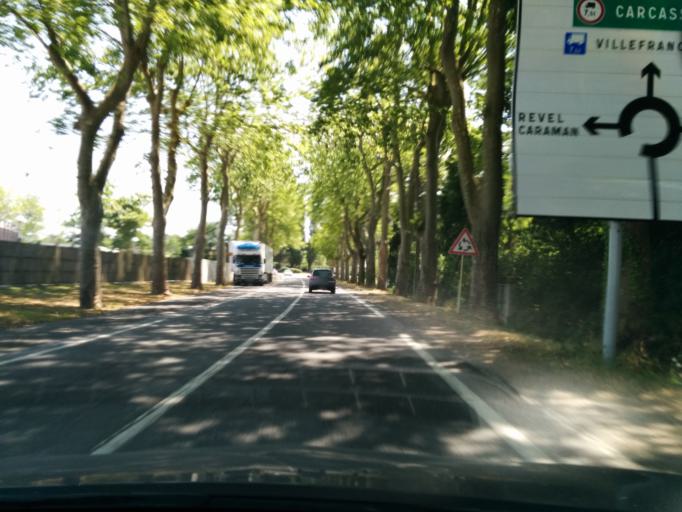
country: FR
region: Midi-Pyrenees
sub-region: Departement de la Haute-Garonne
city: Villefranche-de-Lauragais
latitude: 43.4072
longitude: 1.7077
